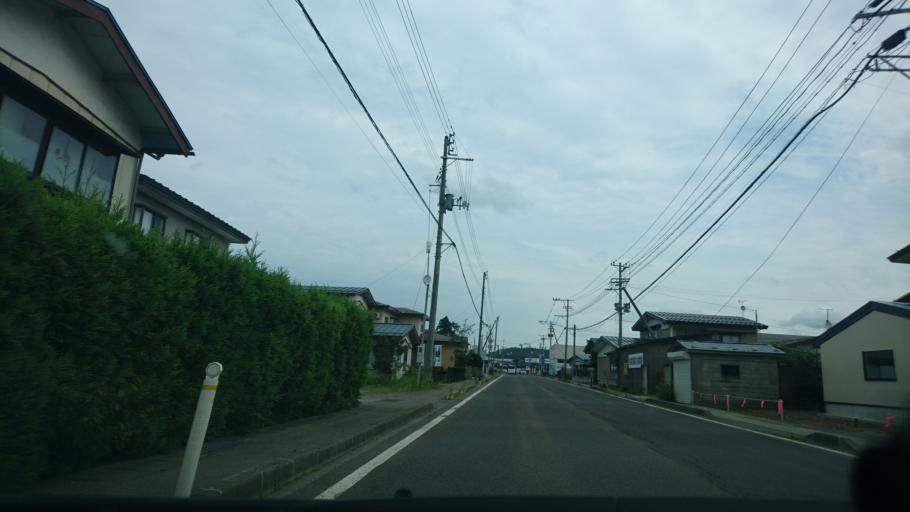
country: JP
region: Akita
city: Yuzawa
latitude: 39.1833
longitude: 140.4976
